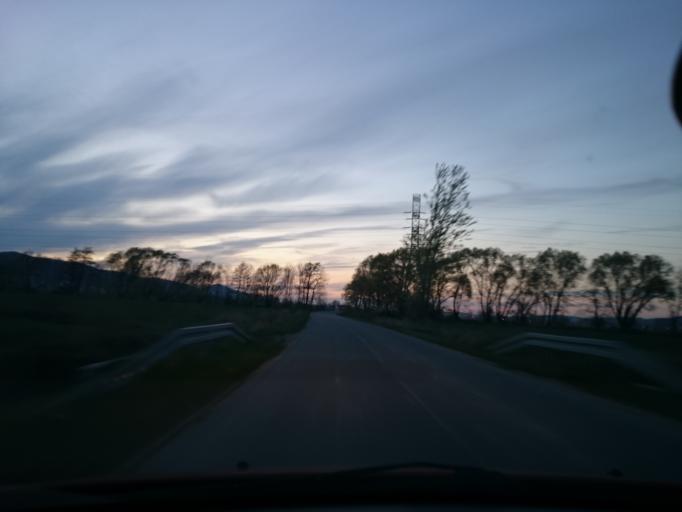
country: PL
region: Lower Silesian Voivodeship
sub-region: Powiat zabkowicki
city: Budzow
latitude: 50.5670
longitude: 16.6848
